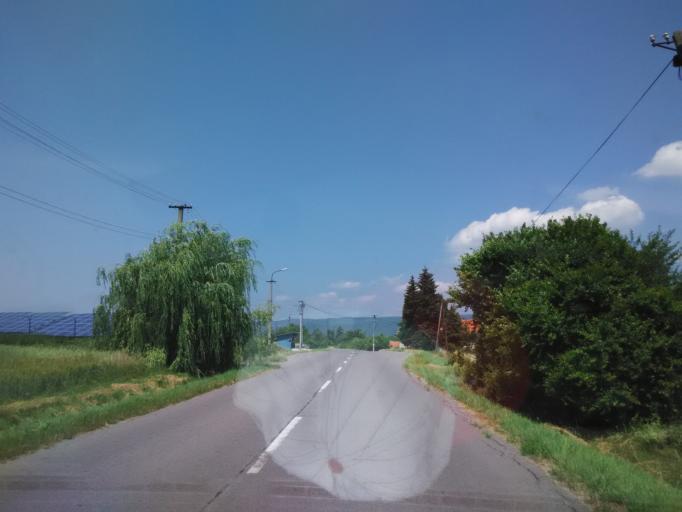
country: SK
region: Nitriansky
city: Levice
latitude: 48.2819
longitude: 18.6914
